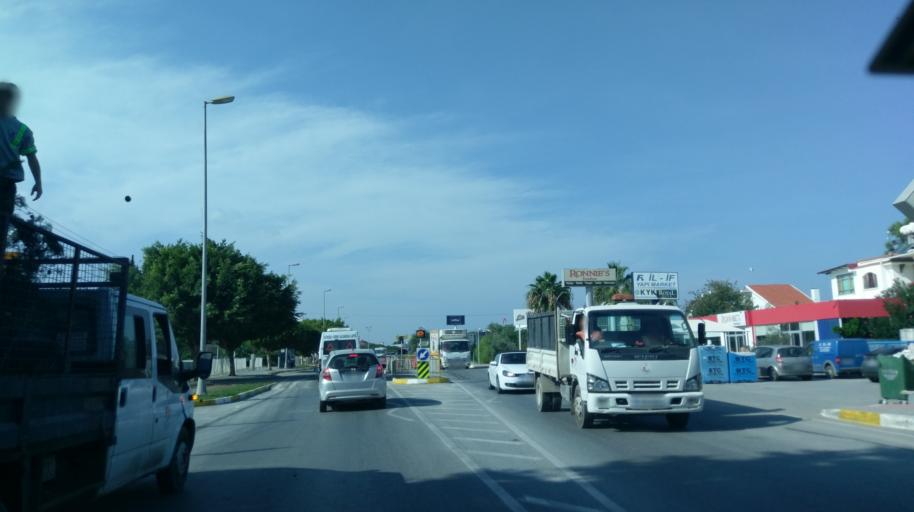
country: CY
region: Keryneia
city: Kyrenia
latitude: 35.3401
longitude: 33.2905
